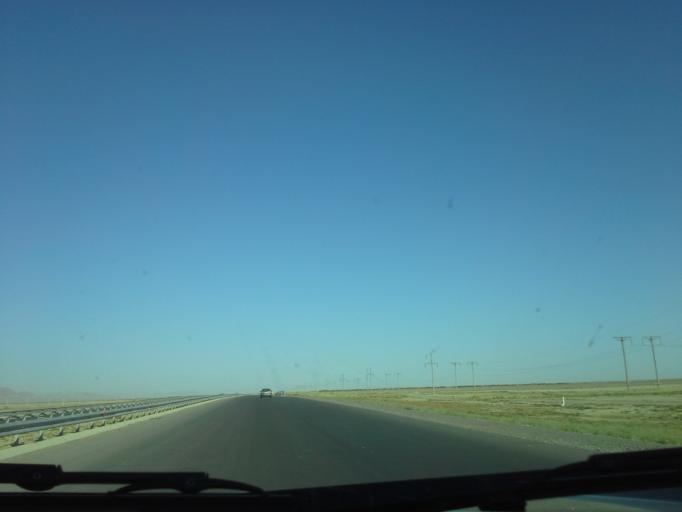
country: TM
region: Balkan
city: Serdar
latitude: 39.0254
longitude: 56.1962
